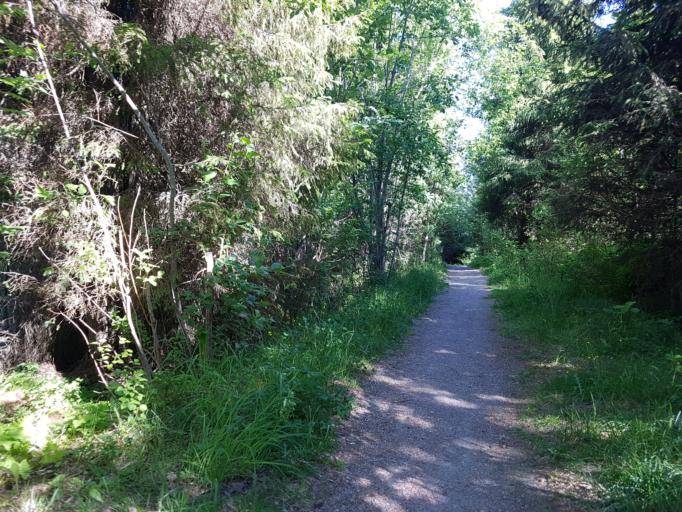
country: NO
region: Sor-Trondelag
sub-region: Trondheim
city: Trondheim
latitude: 63.3971
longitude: 10.3241
